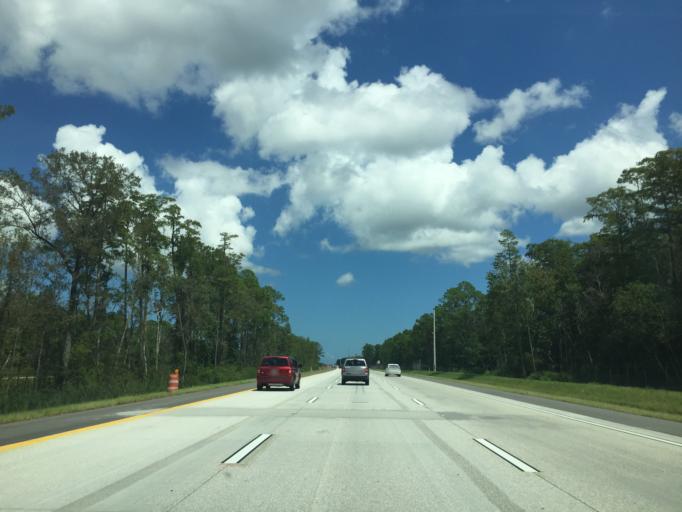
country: US
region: Florida
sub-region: Volusia County
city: Samsula-Spruce Creek
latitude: 29.0900
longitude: -81.1630
